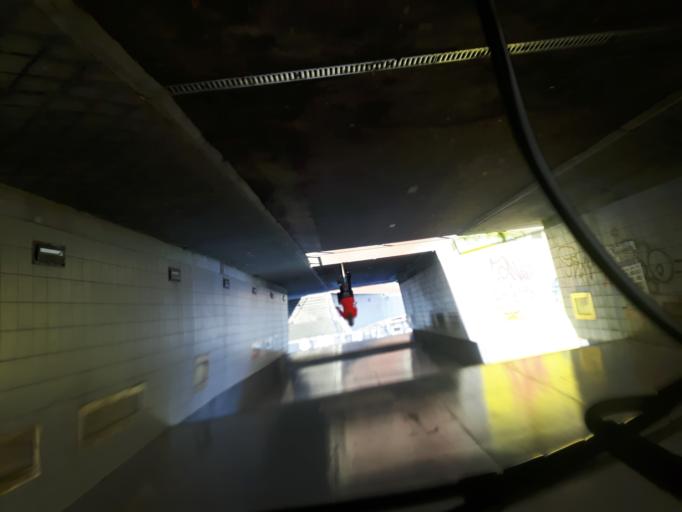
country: NL
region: Zeeland
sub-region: Gemeente Middelburg
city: Middelburg
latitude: 51.4959
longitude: 3.6206
